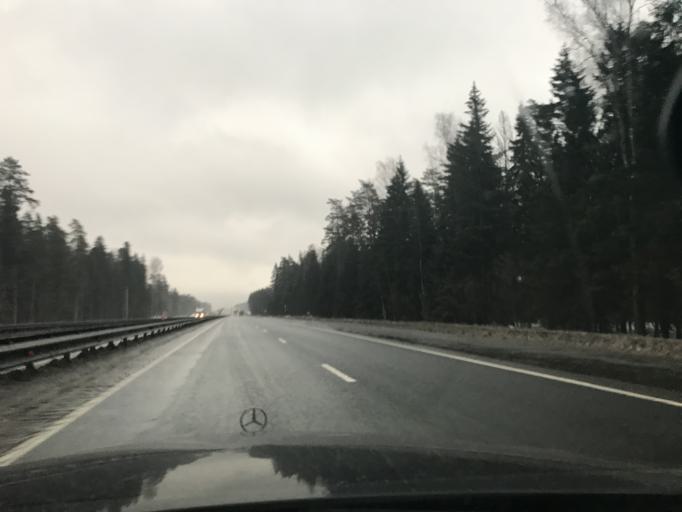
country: RU
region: Vladimir
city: Krasnyy Oktyabr'
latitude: 56.2169
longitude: 41.4285
